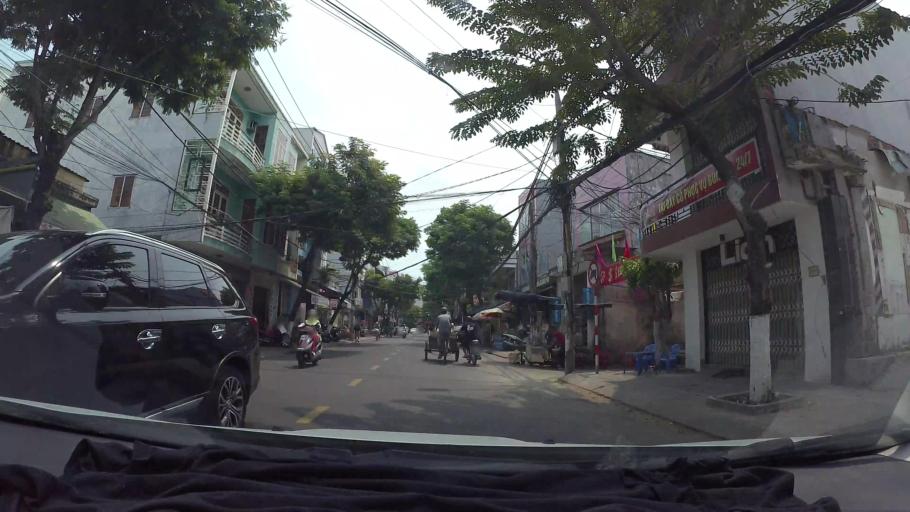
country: VN
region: Da Nang
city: Da Nang
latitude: 16.0775
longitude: 108.2148
